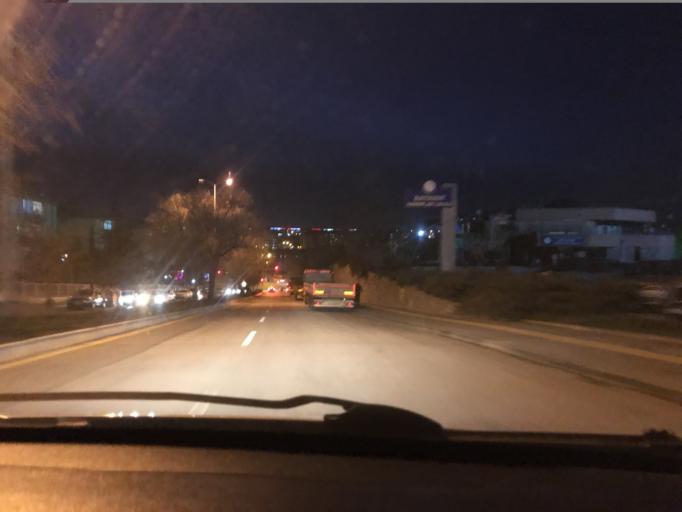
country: TR
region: Ankara
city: Batikent
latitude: 39.9610
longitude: 32.7343
